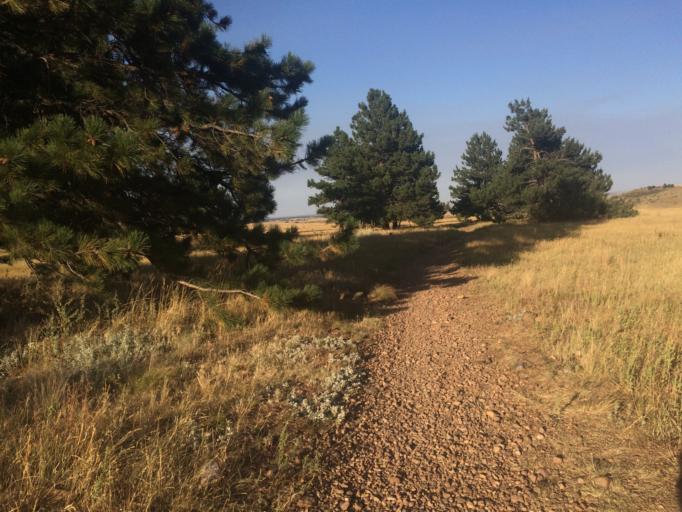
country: US
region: Colorado
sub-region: Boulder County
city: Superior
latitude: 39.9183
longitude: -105.2445
